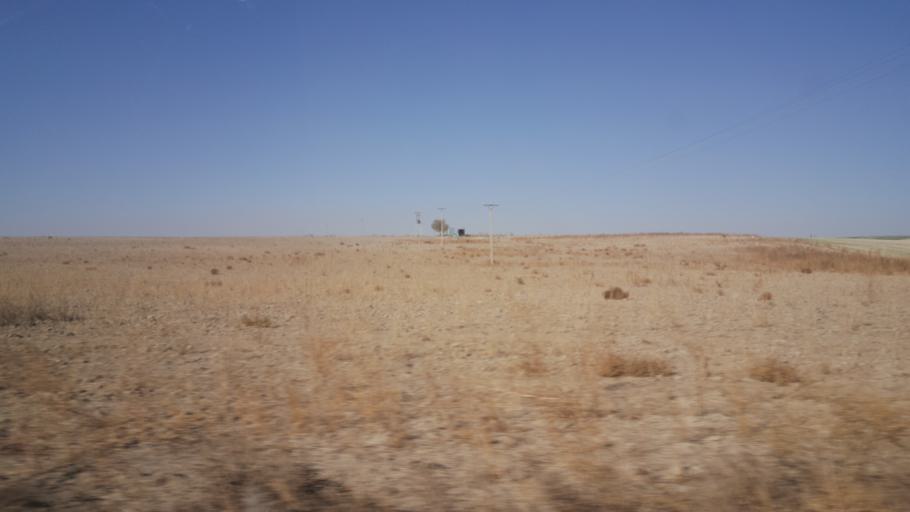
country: TR
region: Konya
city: Celtik
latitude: 39.0629
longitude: 31.8784
